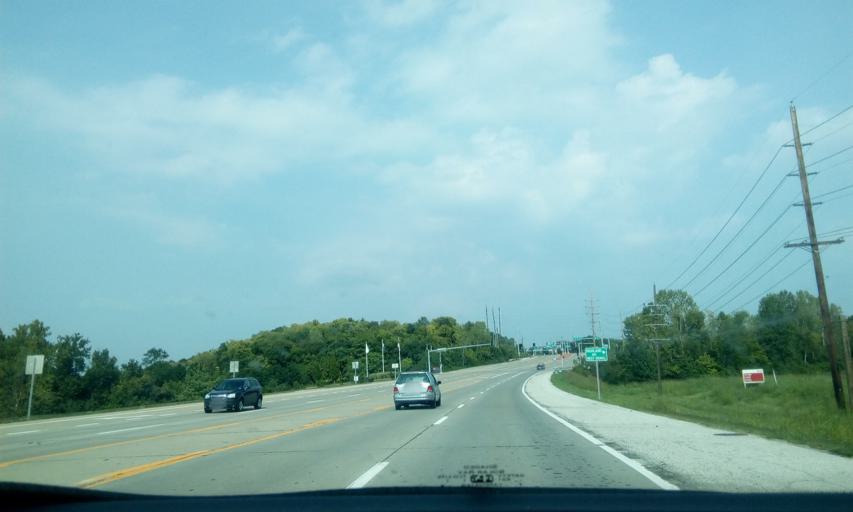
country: US
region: Missouri
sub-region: Saint Louis County
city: Des Peres
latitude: 38.5804
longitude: -90.4530
